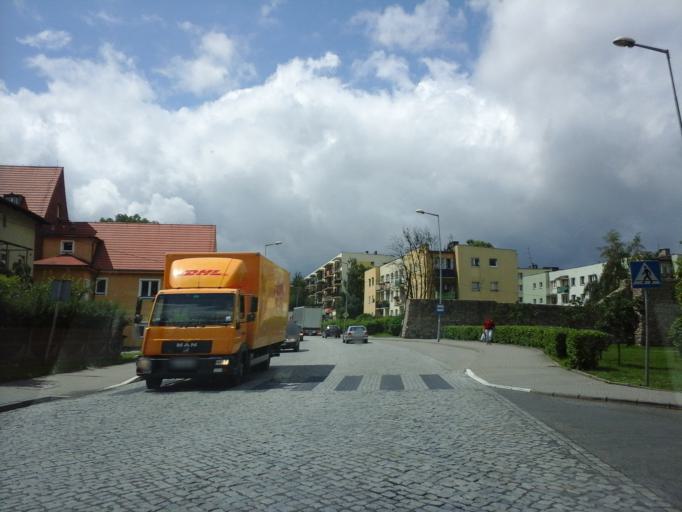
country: PL
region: Lubusz
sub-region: Powiat strzelecko-drezdenecki
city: Strzelce Krajenskie
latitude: 52.8802
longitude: 15.5372
